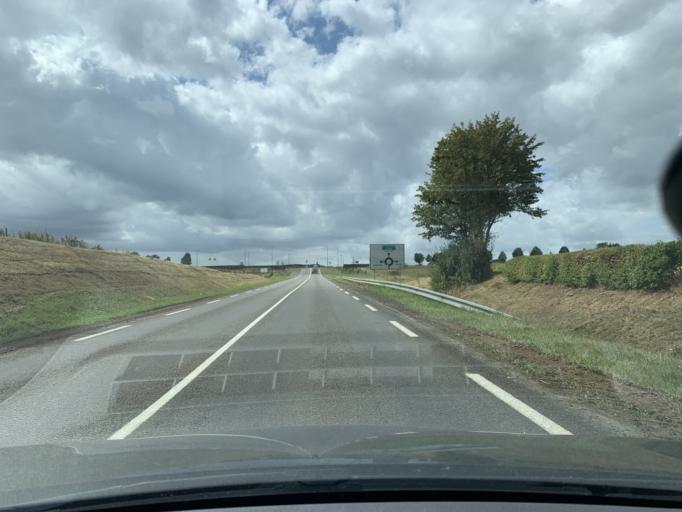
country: FR
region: Picardie
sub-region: Departement de l'Aisne
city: Hirson
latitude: 49.9070
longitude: 4.0989
